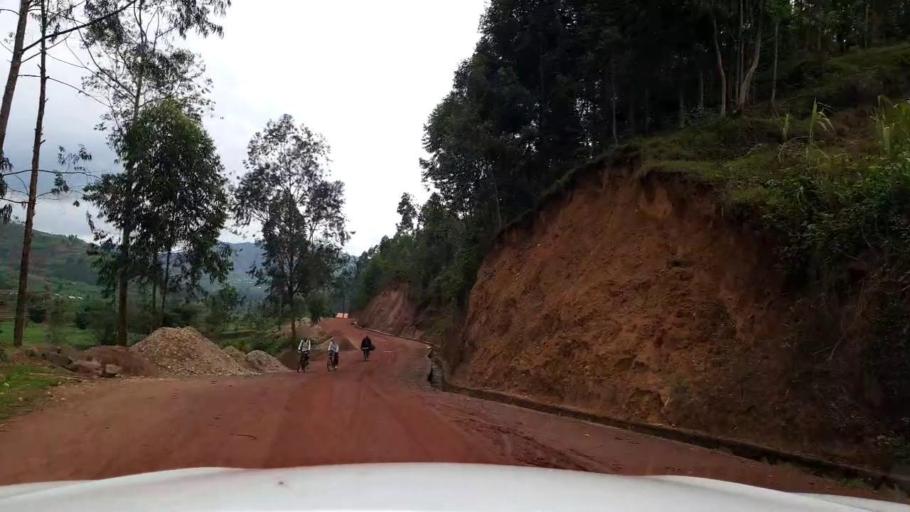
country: RW
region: Northern Province
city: Musanze
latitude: -1.6710
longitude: 29.8003
